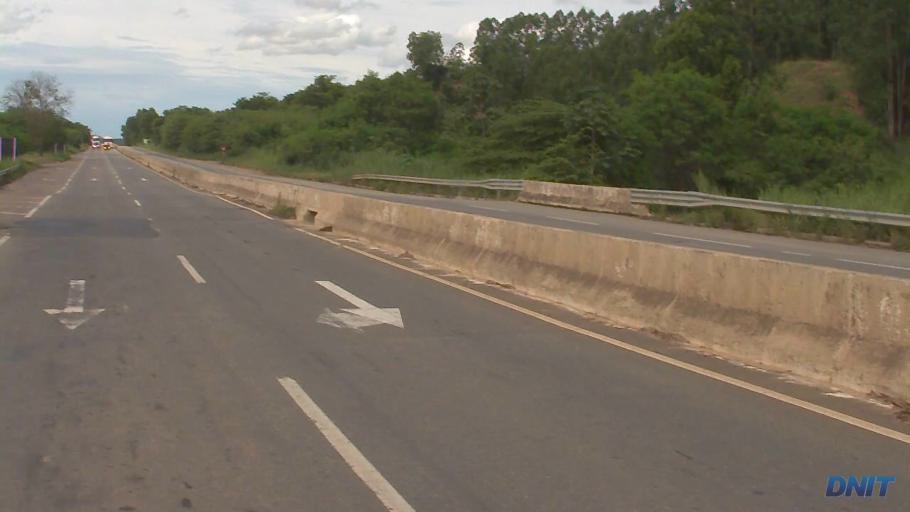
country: BR
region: Minas Gerais
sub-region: Ipaba
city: Ipaba
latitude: -19.3212
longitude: -42.4061
